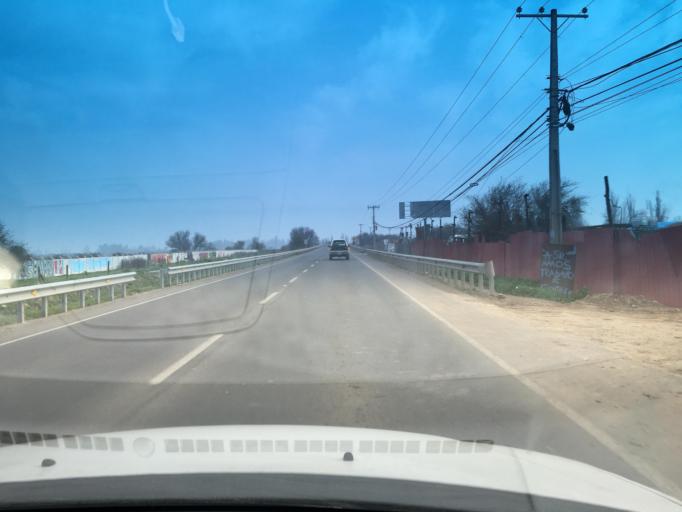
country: CL
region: Santiago Metropolitan
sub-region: Provincia de Chacabuco
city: Lampa
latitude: -33.3283
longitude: -70.8242
